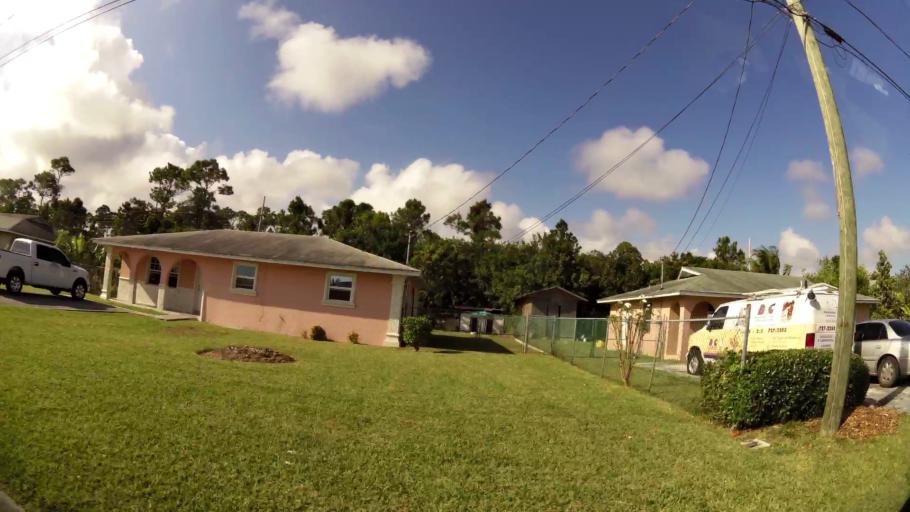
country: BS
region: Freeport
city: Lucaya
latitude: 26.5232
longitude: -78.6678
